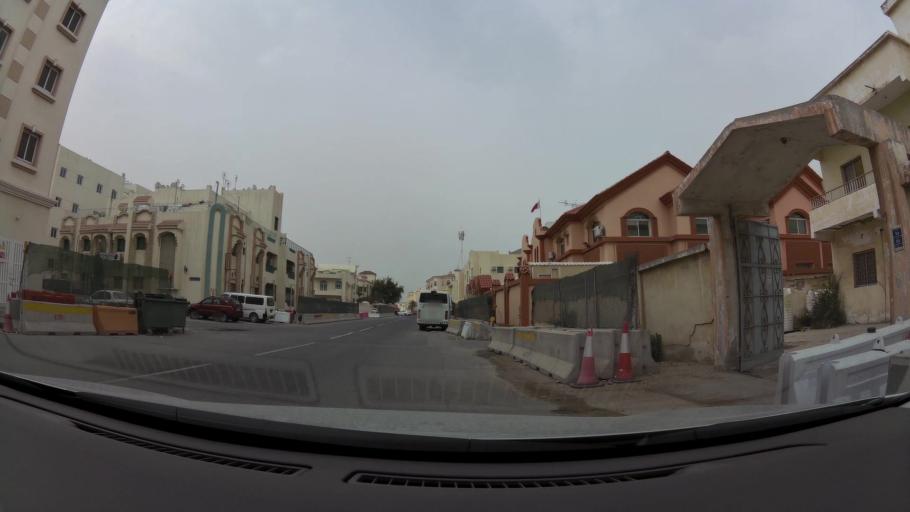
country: QA
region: Baladiyat ad Dawhah
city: Doha
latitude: 25.2534
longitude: 51.5570
